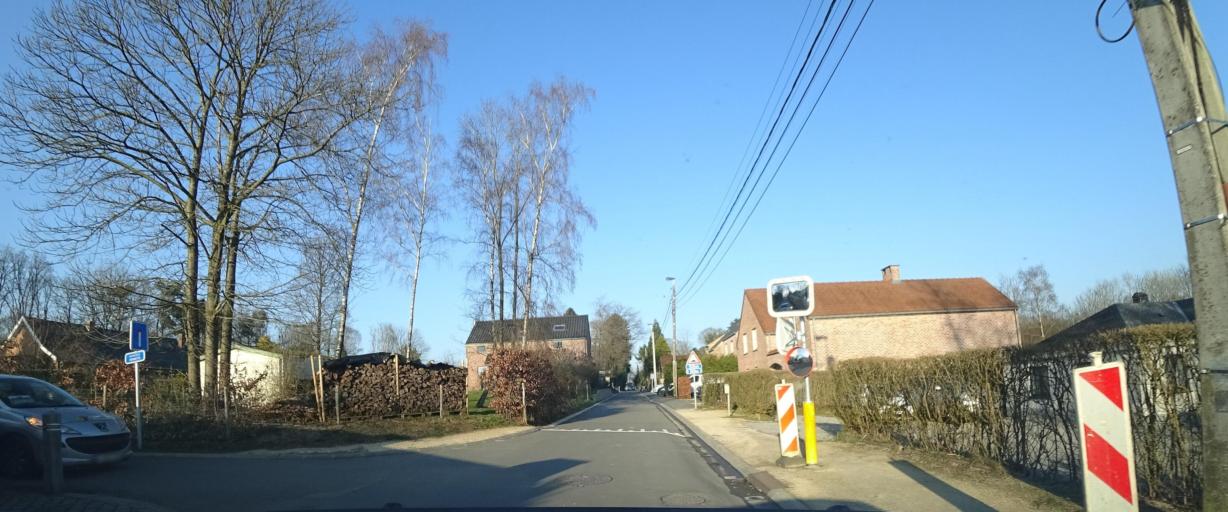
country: BE
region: Wallonia
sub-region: Province du Brabant Wallon
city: Ottignies
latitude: 50.6481
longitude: 4.5313
